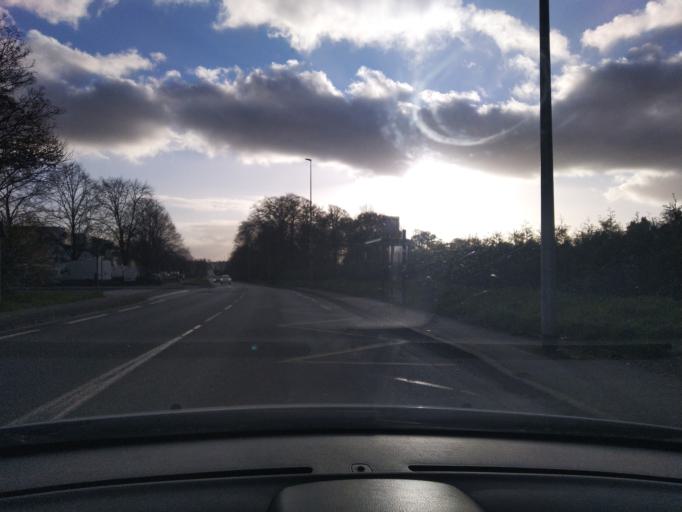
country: FR
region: Brittany
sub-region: Departement du Finistere
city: Morlaix
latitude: 48.5873
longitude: -3.8145
